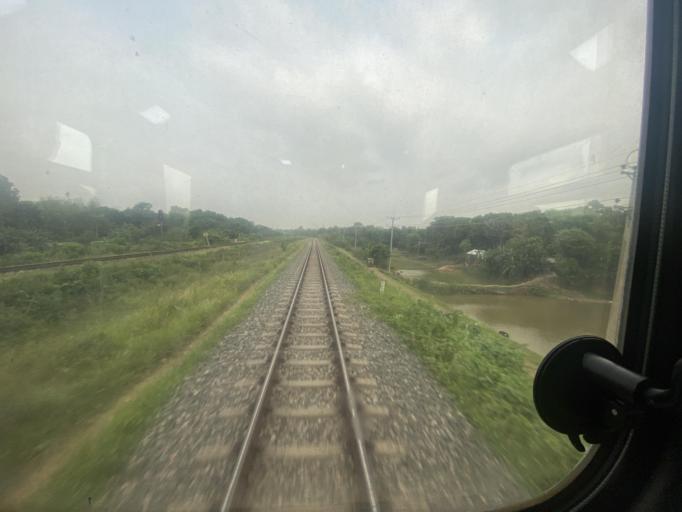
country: BD
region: Dhaka
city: Tungi
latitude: 23.9357
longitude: 90.4881
